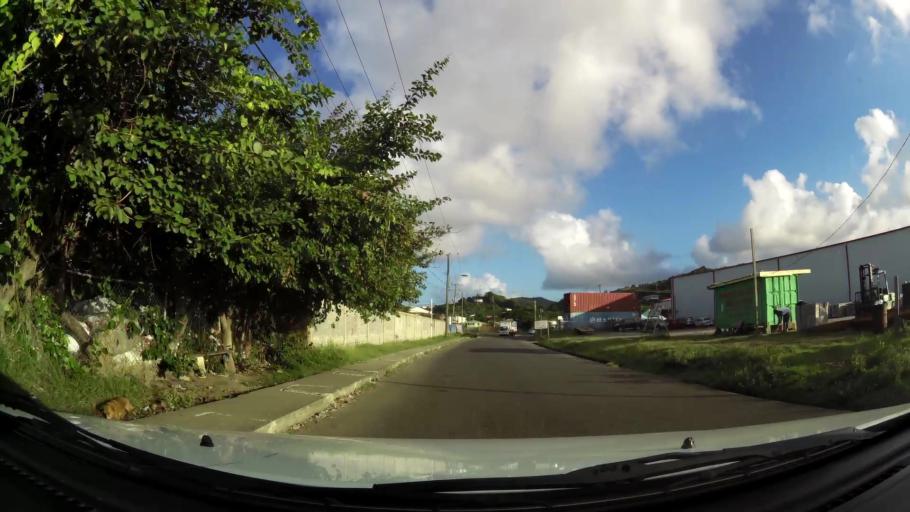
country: LC
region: Gros-Islet
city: Gros Islet
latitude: 14.0793
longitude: -60.9458
